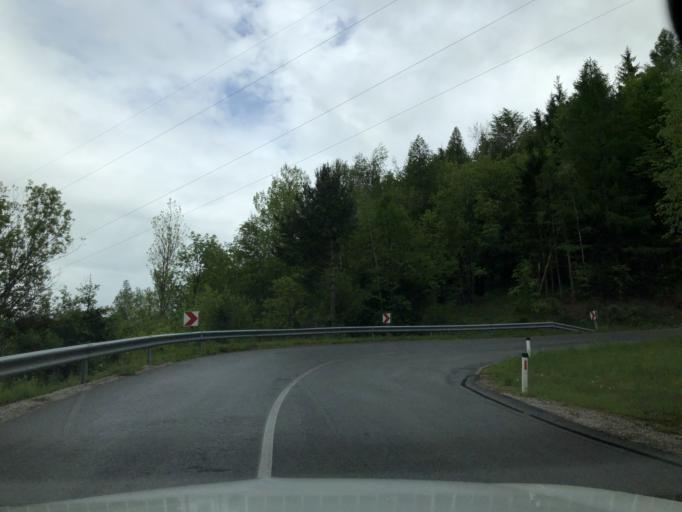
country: SI
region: Jesenice
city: Slovenski Javornik
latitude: 46.4141
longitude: 14.0909
